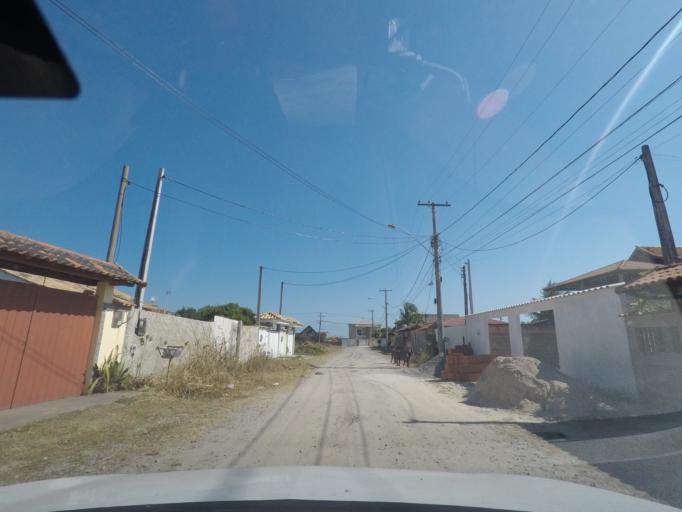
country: BR
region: Rio de Janeiro
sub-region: Marica
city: Marica
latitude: -22.9683
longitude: -42.9083
